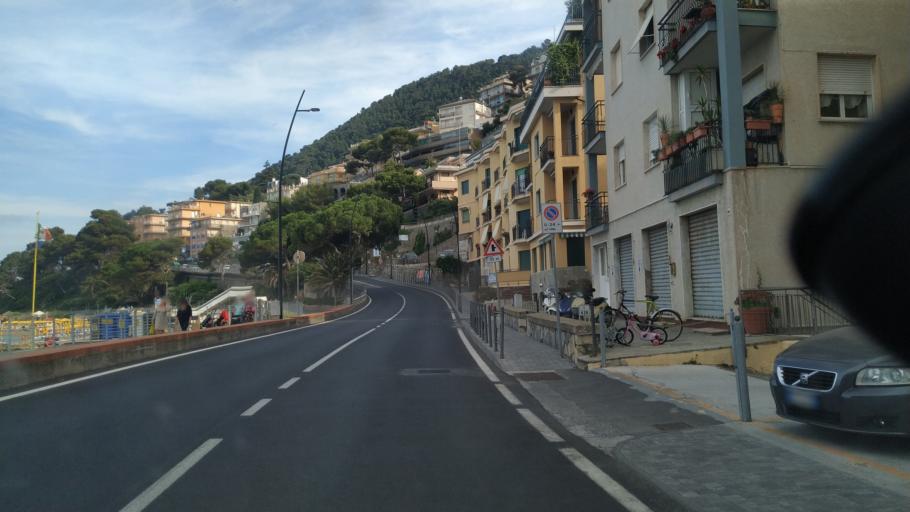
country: IT
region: Liguria
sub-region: Provincia di Savona
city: Laigueglia
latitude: 43.9708
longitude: 8.1607
